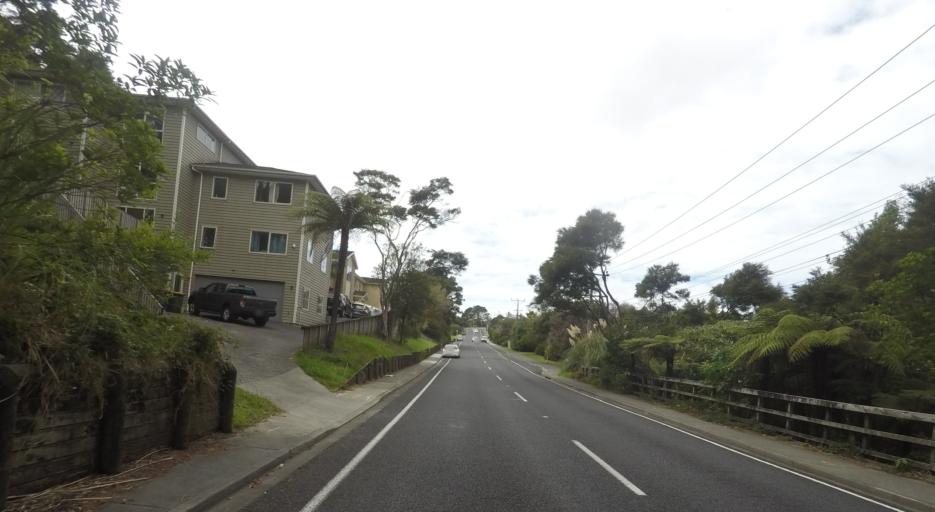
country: NZ
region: Auckland
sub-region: Auckland
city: North Shore
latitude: -36.7708
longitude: 174.6923
